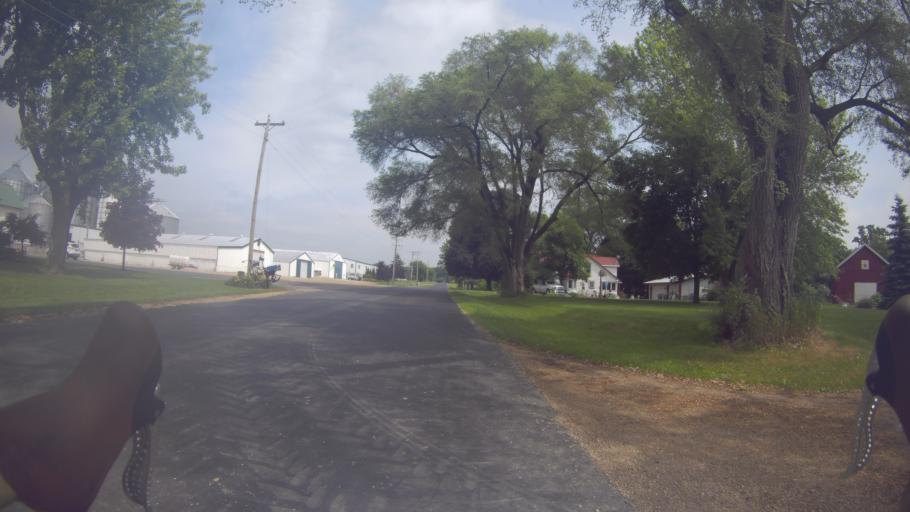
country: US
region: Wisconsin
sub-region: Rock County
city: Edgerton
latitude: 42.8899
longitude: -89.0401
